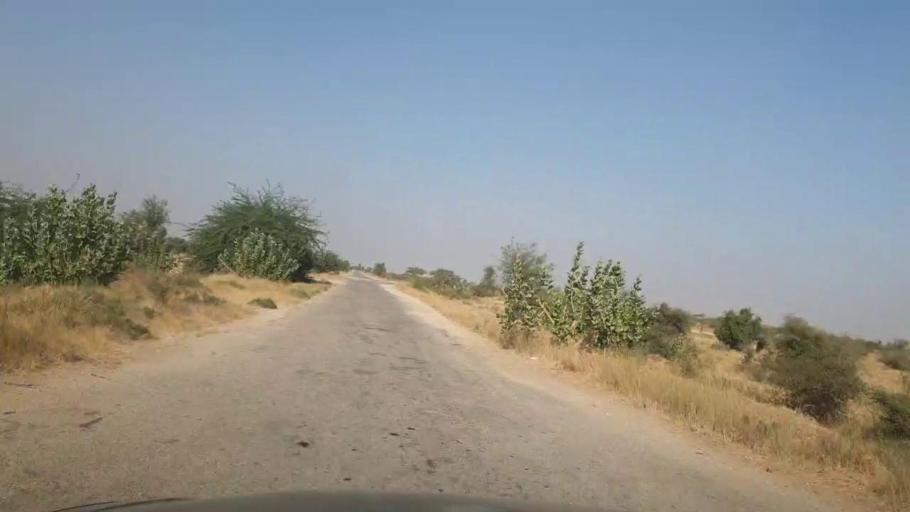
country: PK
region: Sindh
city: Jamshoro
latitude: 25.4792
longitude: 67.8226
